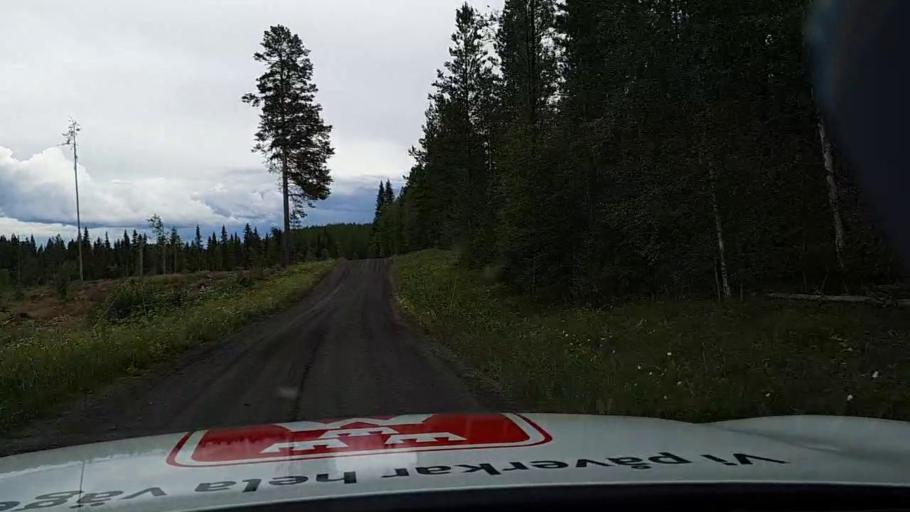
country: SE
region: Jaemtland
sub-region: OEstersunds Kommun
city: Lit
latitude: 63.5617
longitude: 14.7274
